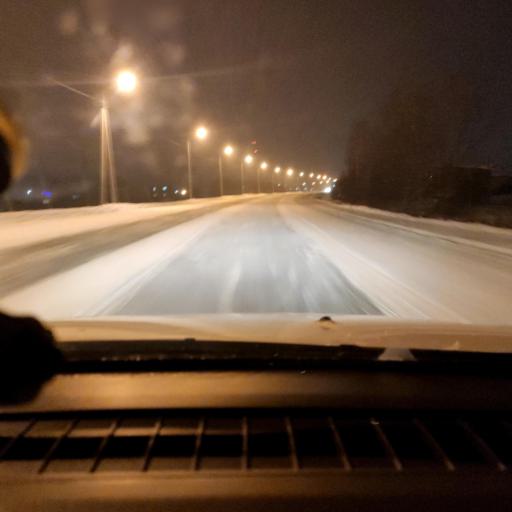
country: RU
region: Samara
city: Georgiyevka
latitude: 53.2679
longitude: 51.0072
